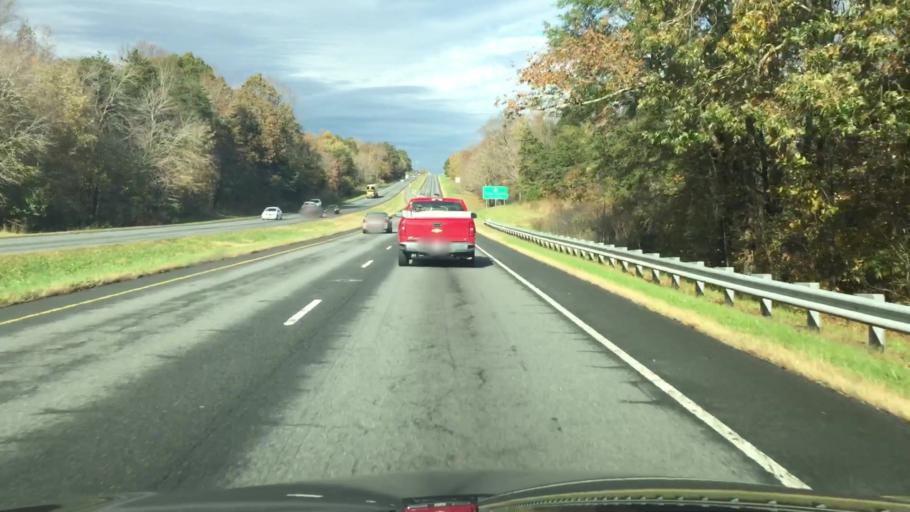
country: US
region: North Carolina
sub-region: Guilford County
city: McLeansville
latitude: 36.2028
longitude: -79.6950
